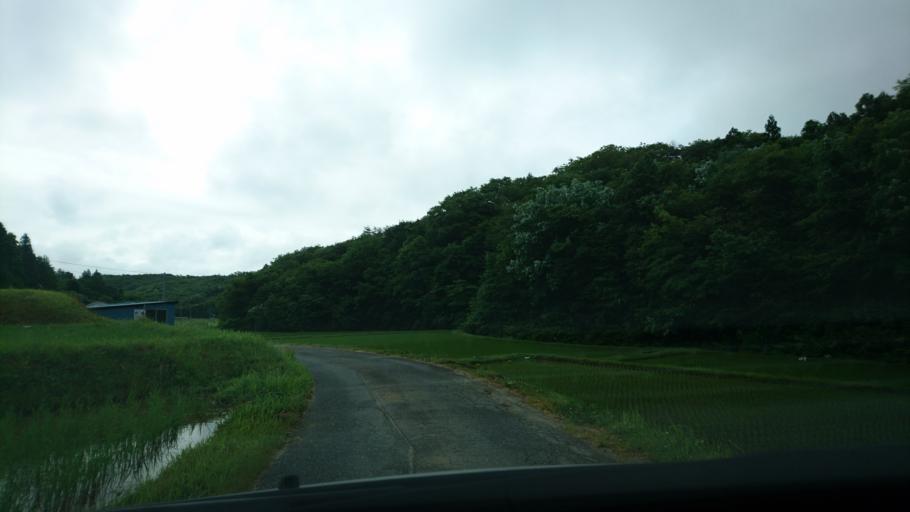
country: JP
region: Iwate
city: Ichinoseki
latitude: 38.8975
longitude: 141.1454
